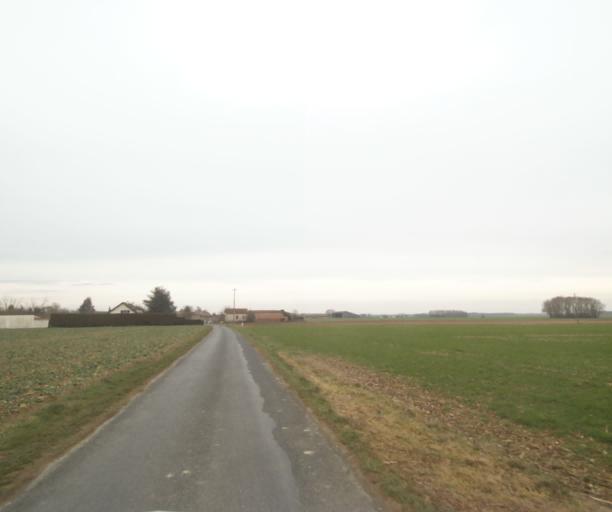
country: FR
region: Champagne-Ardenne
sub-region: Departement de la Haute-Marne
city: Villiers-en-Lieu
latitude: 48.6336
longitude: 4.8300
